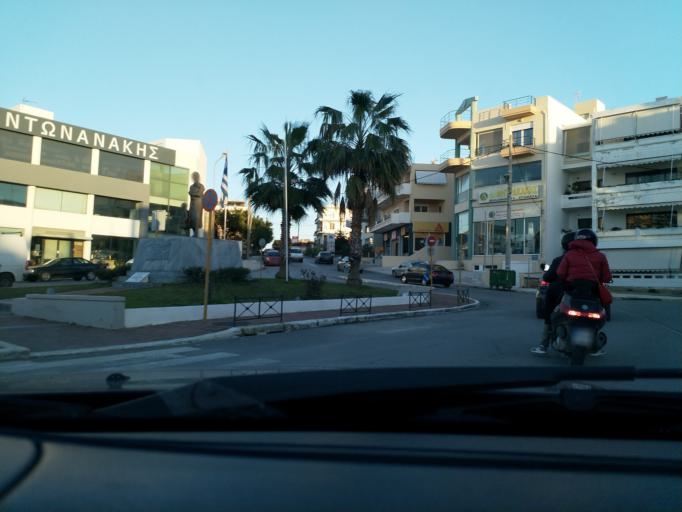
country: GR
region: Crete
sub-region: Nomos Chanias
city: Chania
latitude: 35.5100
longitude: 24.0097
